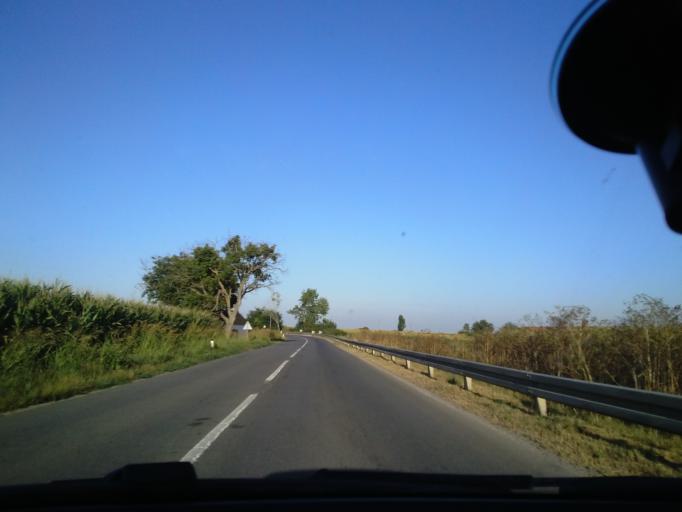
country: RS
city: Maglic
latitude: 45.3905
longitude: 19.4812
